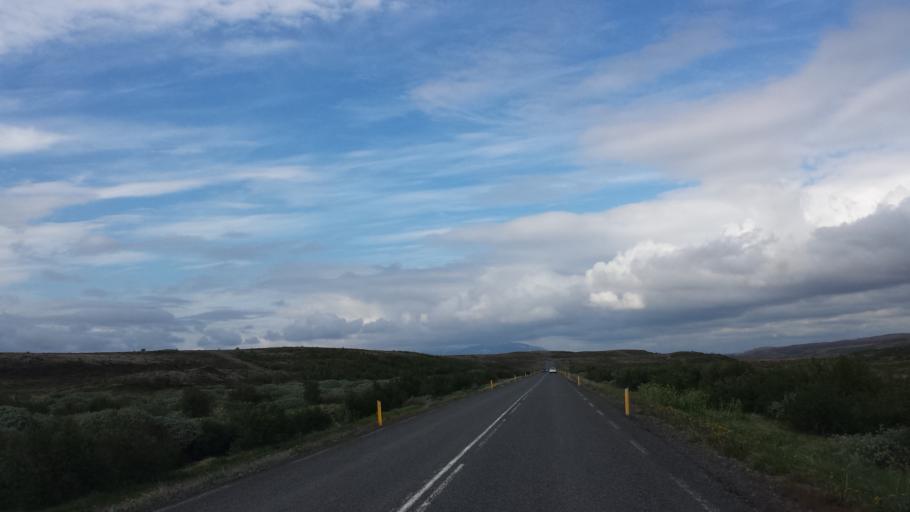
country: IS
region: South
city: Vestmannaeyjar
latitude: 64.3113
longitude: -20.1564
